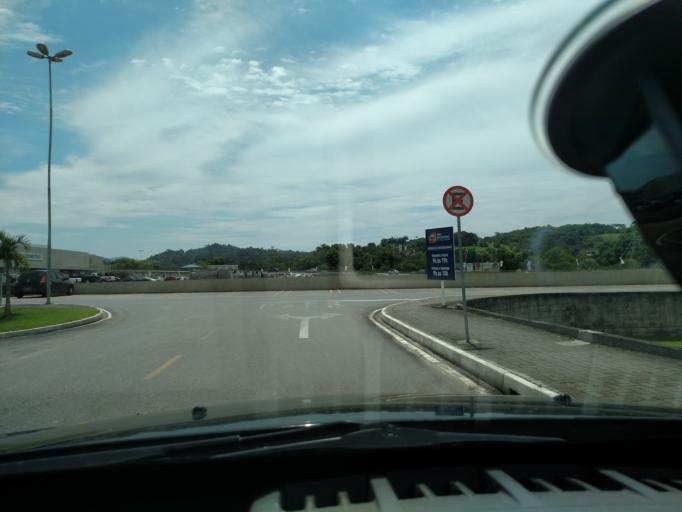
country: BR
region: Santa Catarina
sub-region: Blumenau
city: Blumenau
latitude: -26.8653
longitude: -49.0860
